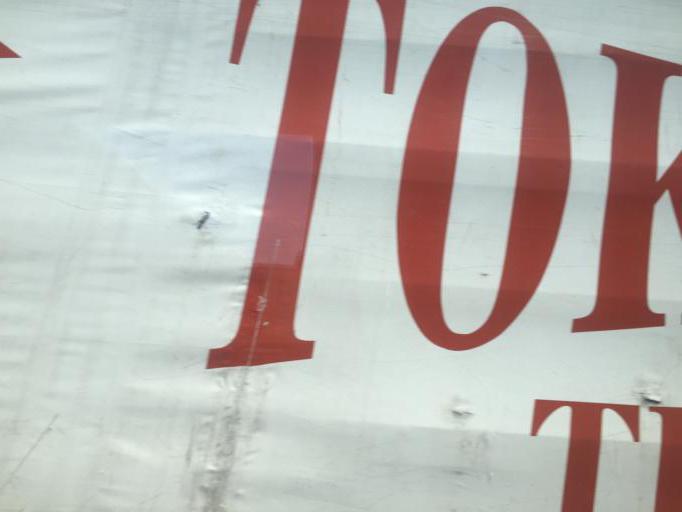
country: TR
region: Diyarbakir
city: Tepe
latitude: 37.8503
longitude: 40.7759
